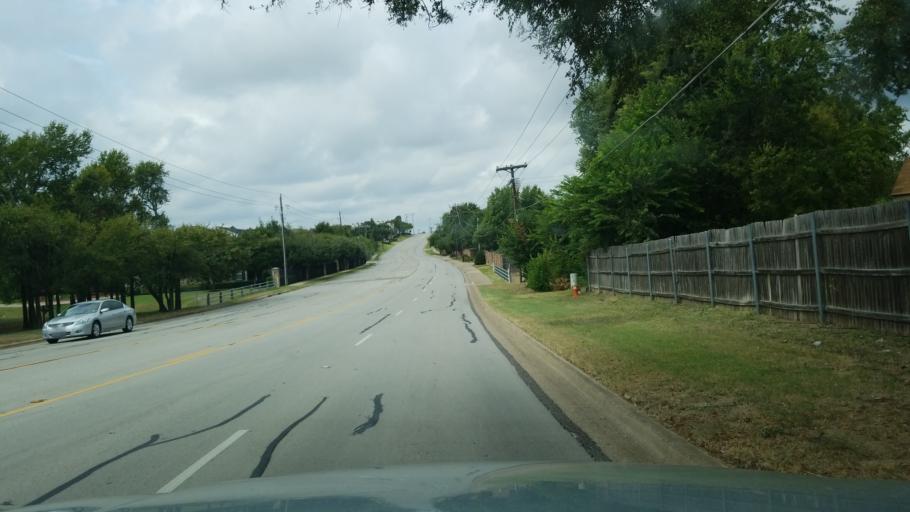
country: US
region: Texas
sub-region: Tarrant County
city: Euless
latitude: 32.8452
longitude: -97.1091
